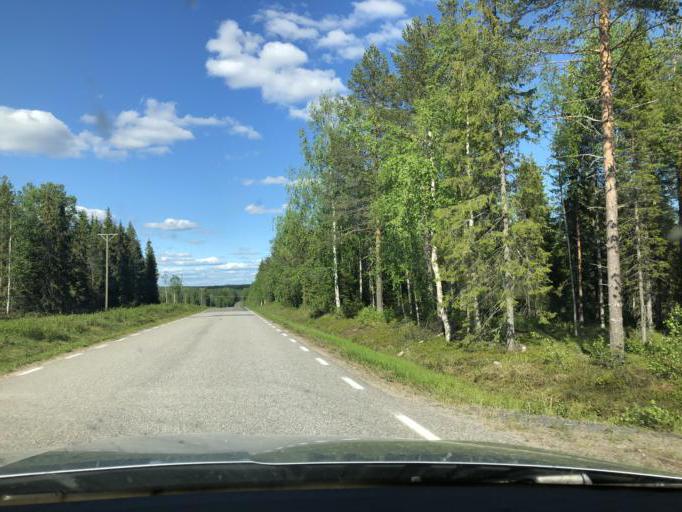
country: SE
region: Norrbotten
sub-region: Kalix Kommun
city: Kalix
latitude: 66.1036
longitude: 23.2815
